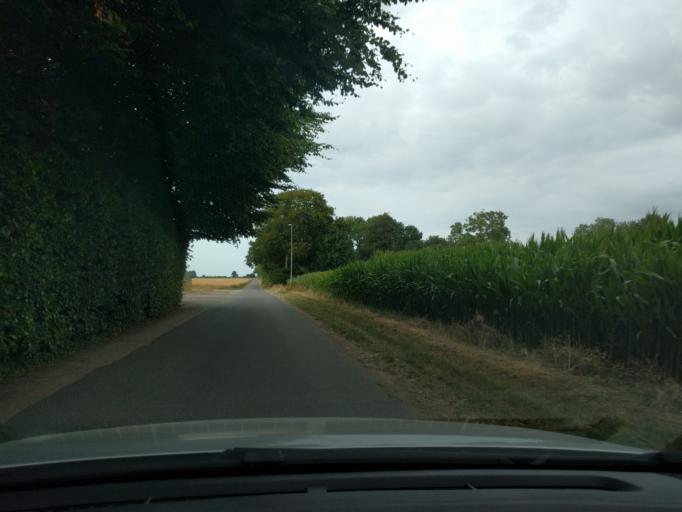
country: DK
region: South Denmark
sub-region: Nordfyns Kommune
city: Otterup
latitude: 55.5745
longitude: 10.4120
